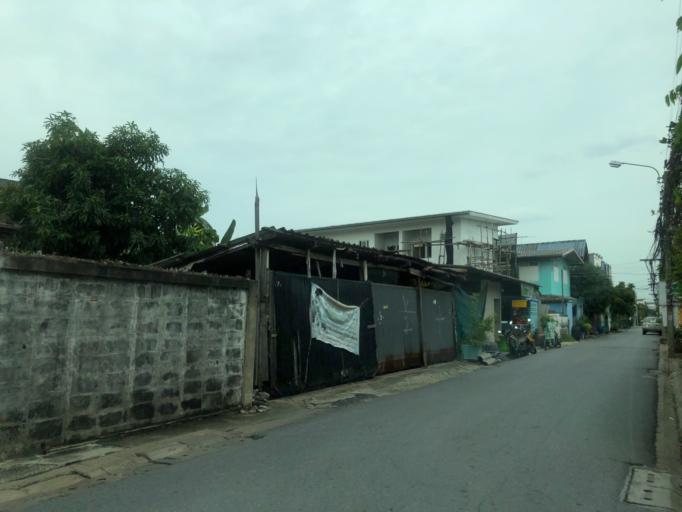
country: TH
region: Bangkok
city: Don Mueang
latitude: 13.9236
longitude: 100.5934
